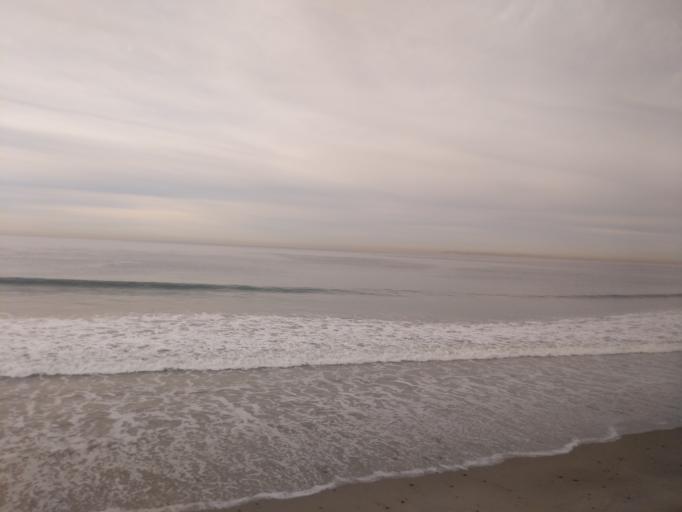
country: US
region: California
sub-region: Orange County
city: San Clemente
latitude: 33.4231
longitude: -117.6233
